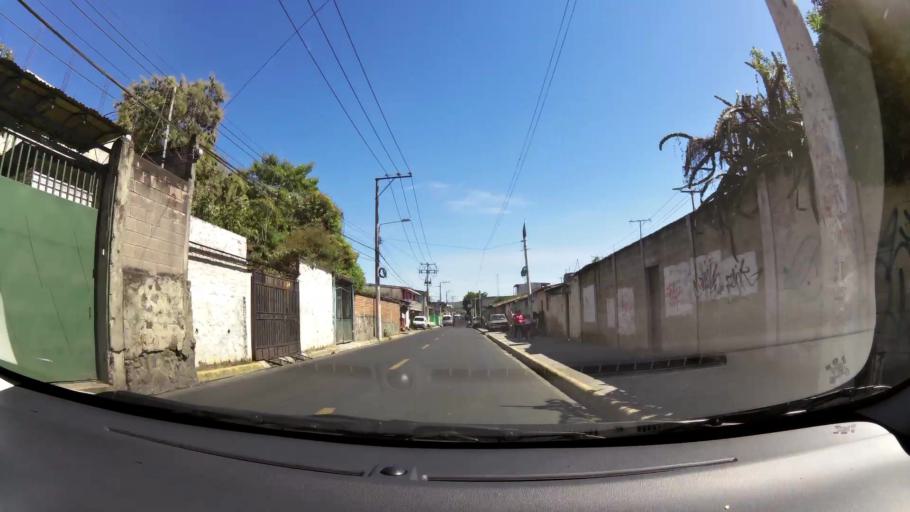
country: SV
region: San Salvador
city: Apopa
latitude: 13.8033
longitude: -89.1813
